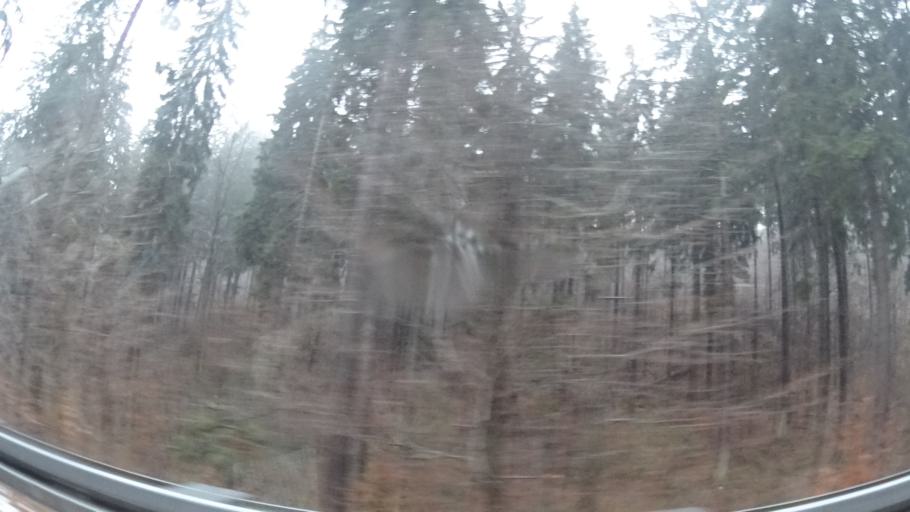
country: DE
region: Thuringia
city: Eisfeld
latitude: 50.4987
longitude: 10.9109
